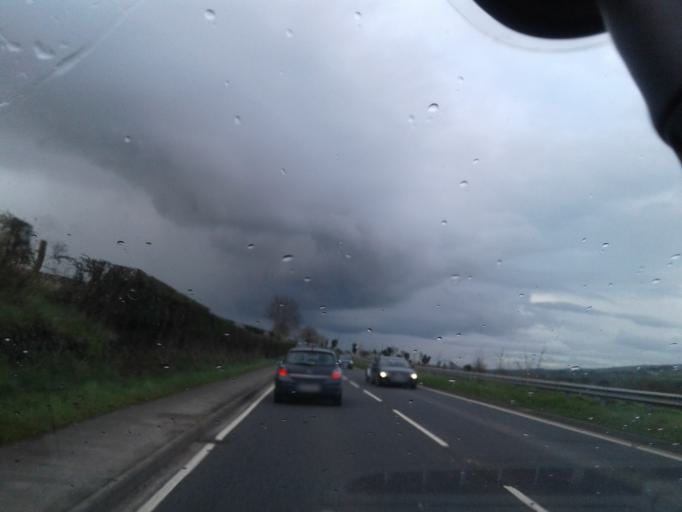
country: GB
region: Northern Ireland
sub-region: Strabane District
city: Sion Mills
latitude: 54.7726
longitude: -7.4661
